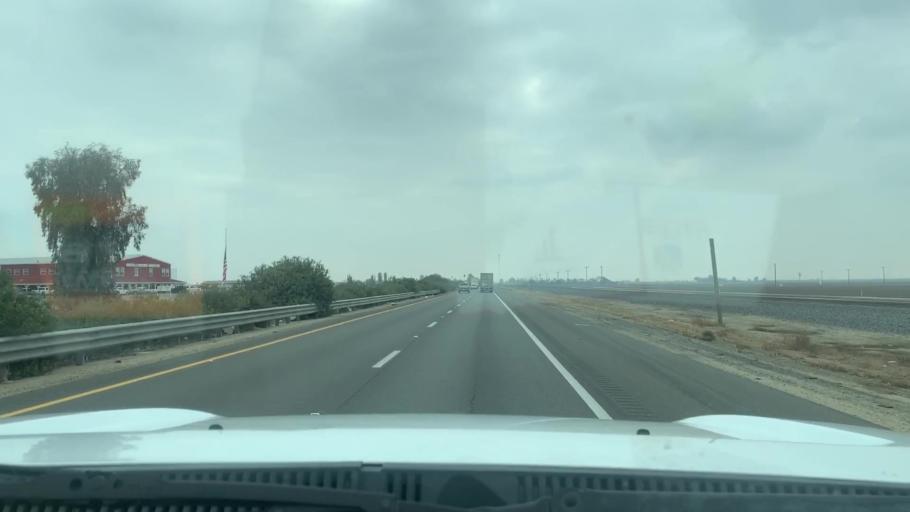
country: US
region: California
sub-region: Tulare County
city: Tipton
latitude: 36.0841
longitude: -119.3201
